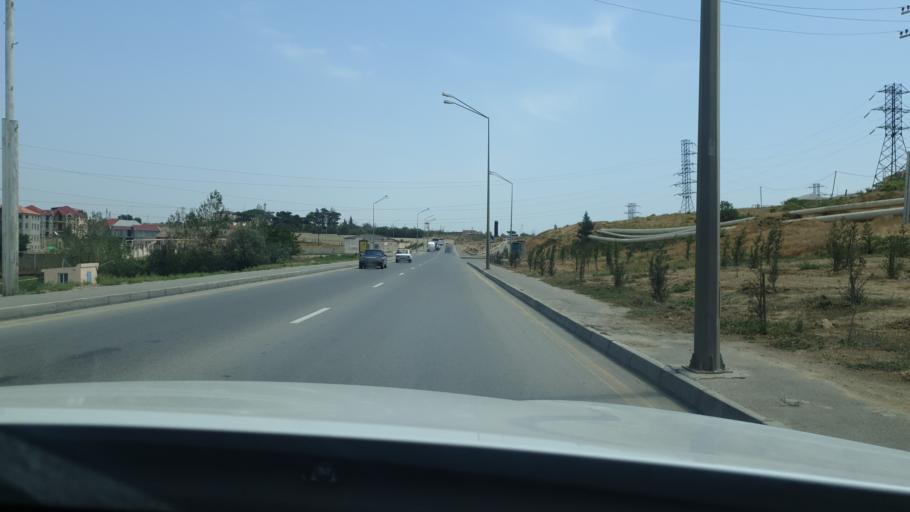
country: AZ
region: Baki
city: Qaracuxur
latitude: 40.3927
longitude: 49.9848
